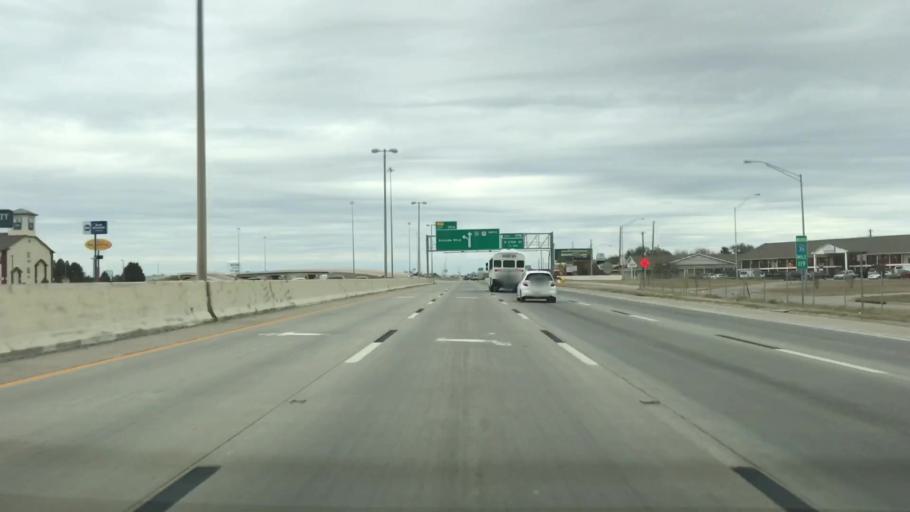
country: US
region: Oklahoma
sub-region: Cleveland County
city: Moore
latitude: 35.3524
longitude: -97.4946
